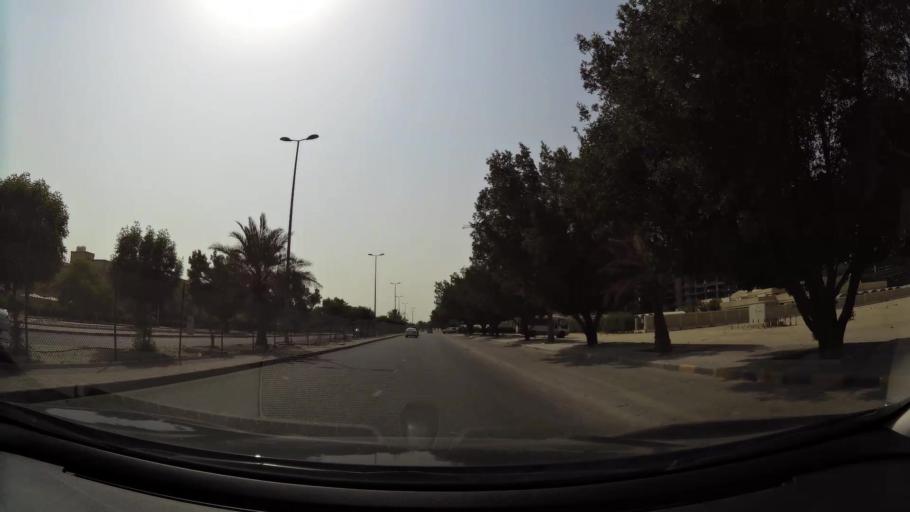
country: KW
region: Muhafazat al Jahra'
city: Al Jahra'
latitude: 29.3383
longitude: 47.6867
